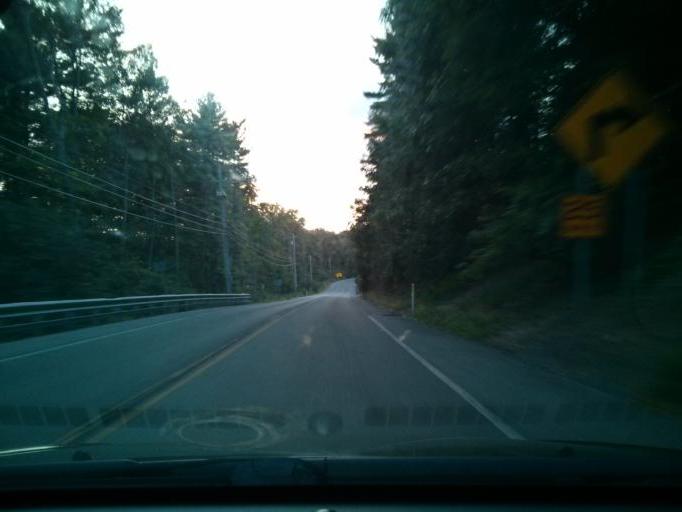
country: US
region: Pennsylvania
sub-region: Centre County
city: State College
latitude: 40.8312
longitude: -77.8806
